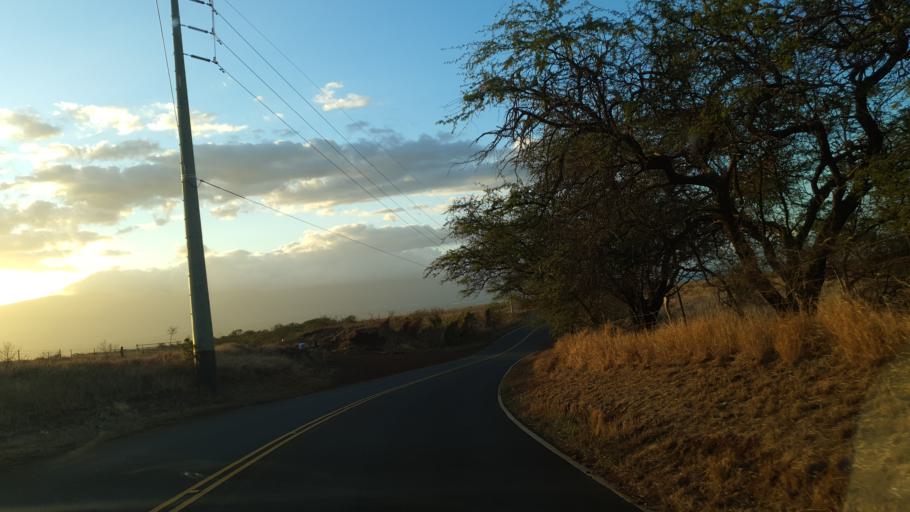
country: US
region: Hawaii
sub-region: Maui County
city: Pukalani
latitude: 20.8027
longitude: -156.3766
